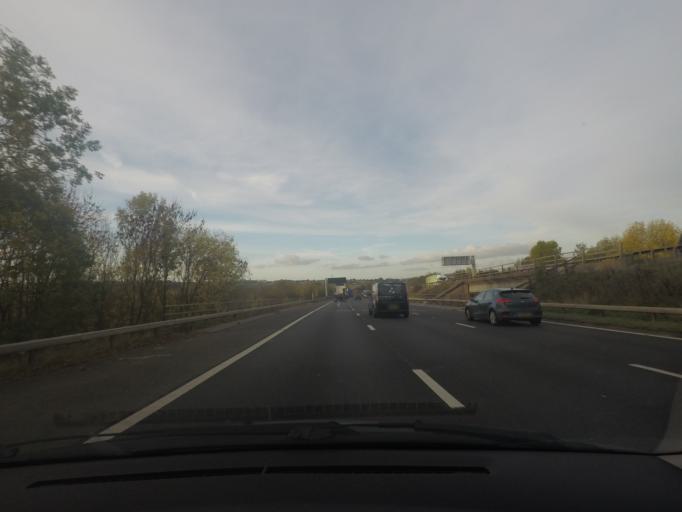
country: GB
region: England
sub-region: Barnsley
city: Darton
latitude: 53.5675
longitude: -1.5407
